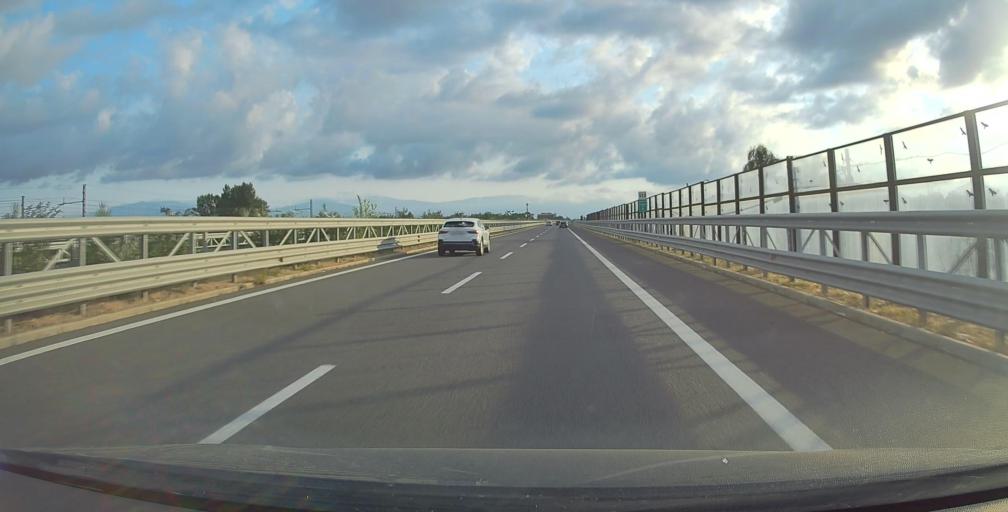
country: IT
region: Calabria
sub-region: Provincia di Catanzaro
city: Acconia
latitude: 38.8334
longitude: 16.2570
